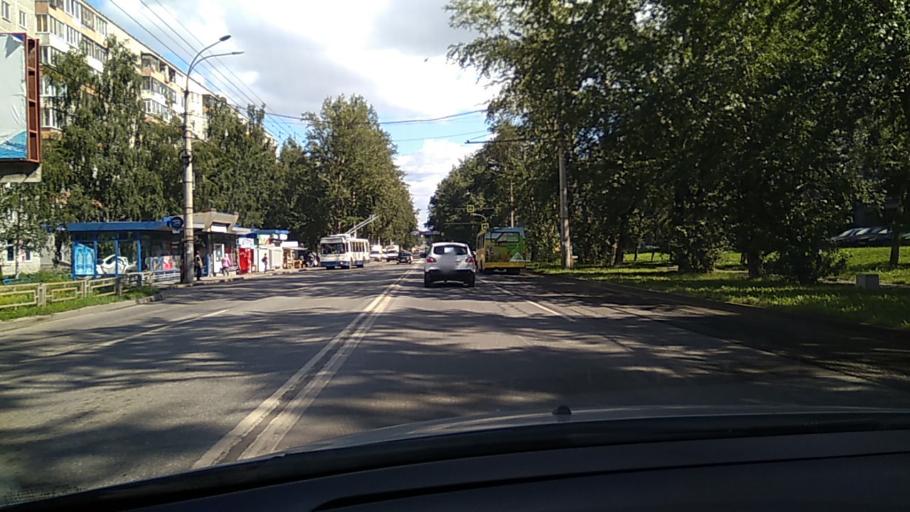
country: RU
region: Sverdlovsk
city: Sovkhoznyy
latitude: 56.7923
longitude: 60.5739
